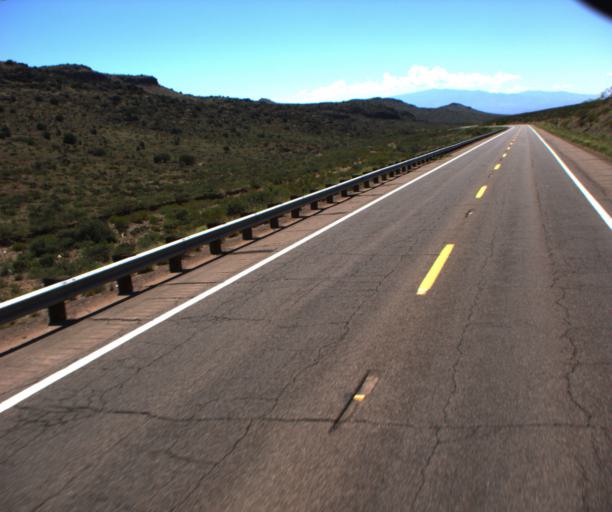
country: US
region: Arizona
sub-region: Greenlee County
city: Clifton
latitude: 32.8467
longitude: -109.3549
